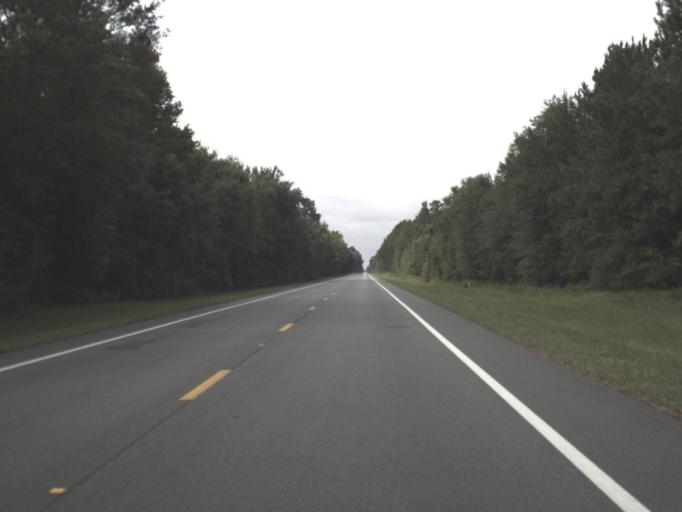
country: US
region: Florida
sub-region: Columbia County
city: Five Points
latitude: 30.4761
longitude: -82.6574
